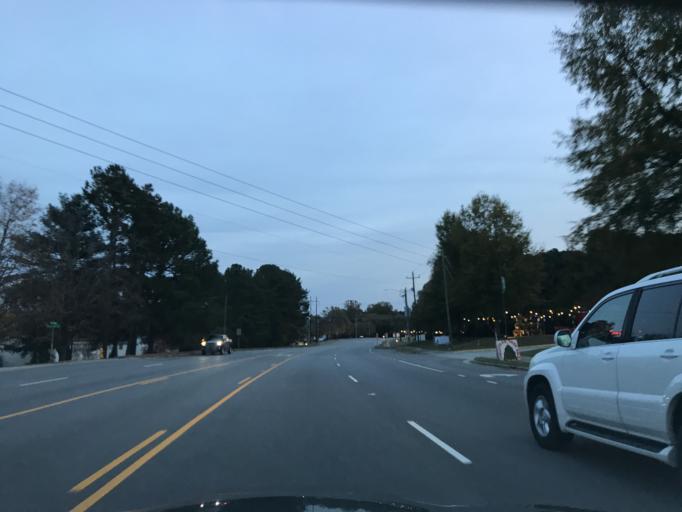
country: US
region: North Carolina
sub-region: Wake County
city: West Raleigh
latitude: 35.8597
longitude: -78.6178
